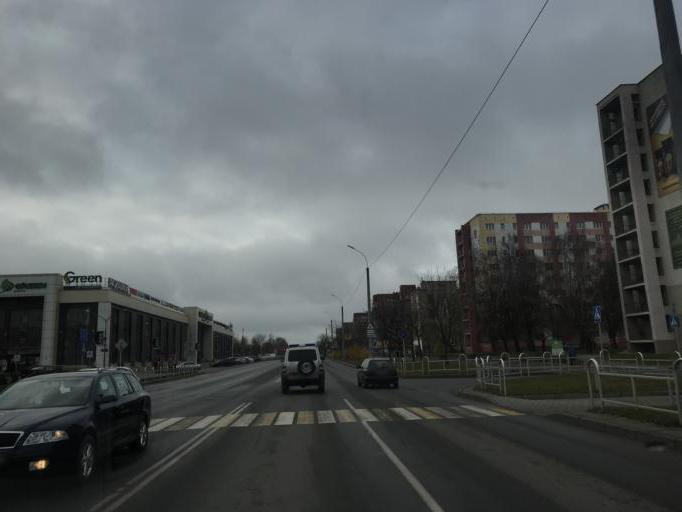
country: BY
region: Mogilev
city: Mahilyow
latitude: 53.8761
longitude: 30.3346
